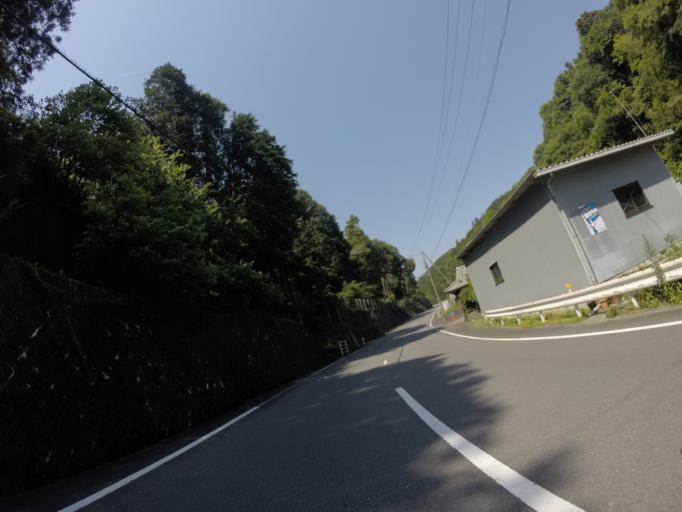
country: JP
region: Shizuoka
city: Fujinomiya
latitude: 35.1407
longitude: 138.5595
